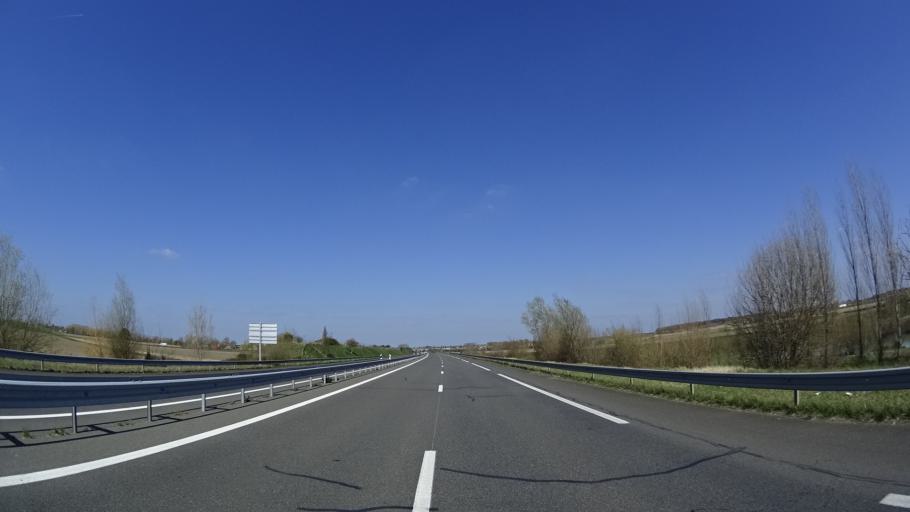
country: FR
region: Pays de la Loire
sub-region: Departement de Maine-et-Loire
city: Saint-Jean
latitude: 47.2650
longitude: -0.3342
